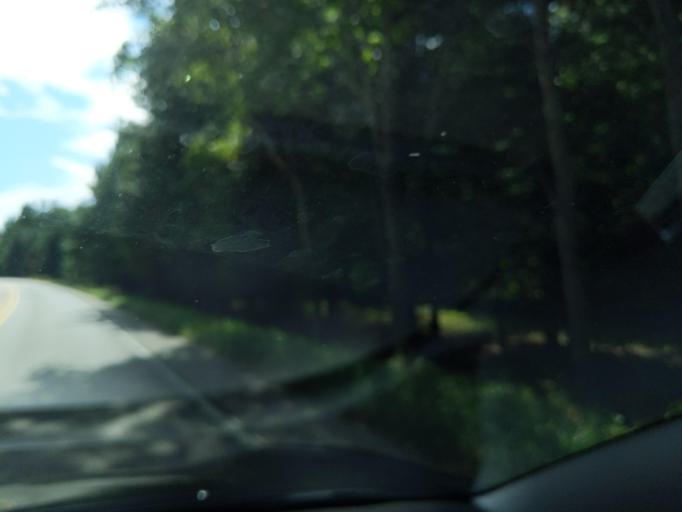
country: US
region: Michigan
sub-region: Antrim County
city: Bellaire
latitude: 45.0622
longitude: -85.3181
